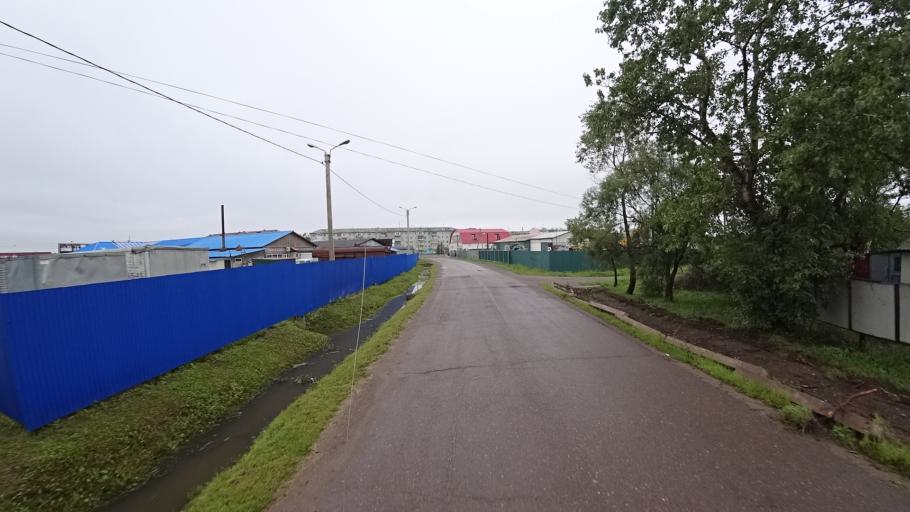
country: RU
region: Primorskiy
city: Monastyrishche
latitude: 44.2045
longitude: 132.4522
